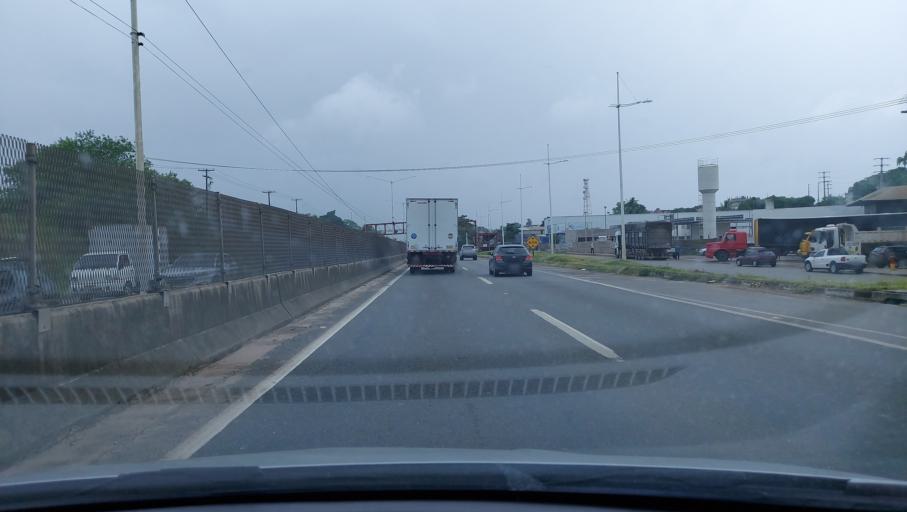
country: BR
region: Bahia
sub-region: Salvador
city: Salvador
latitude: -12.8884
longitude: -38.4417
